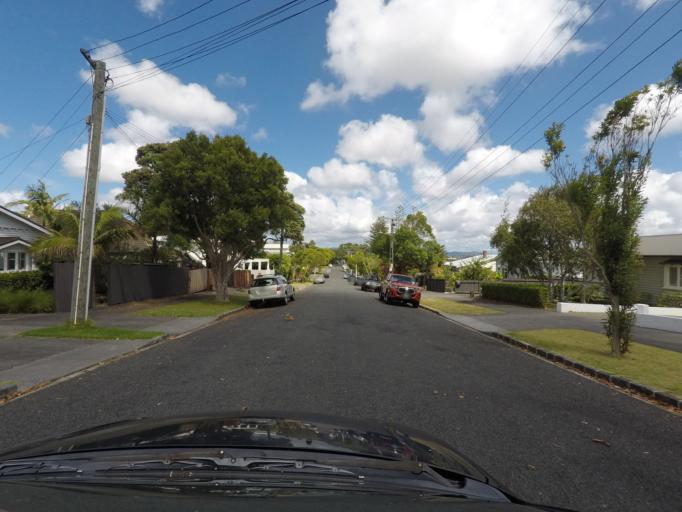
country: NZ
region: Auckland
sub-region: Auckland
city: Rosebank
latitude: -36.8611
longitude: 174.7012
